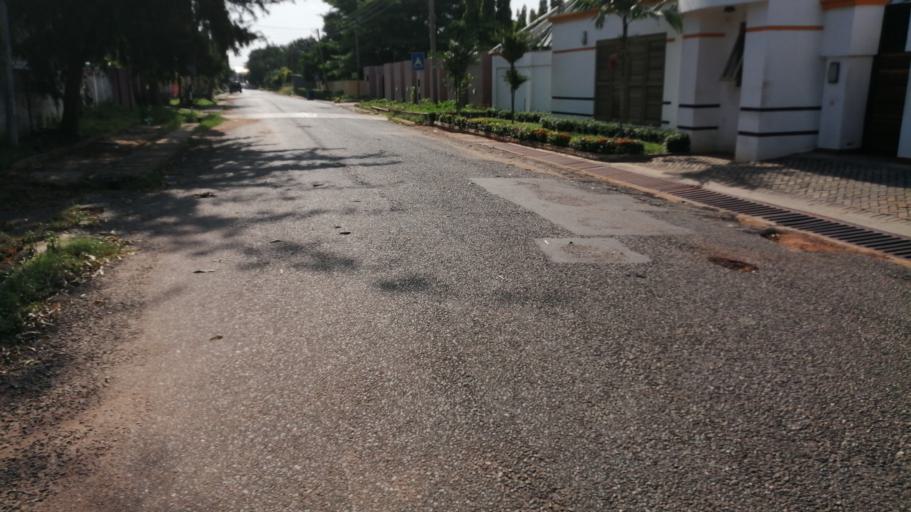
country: GH
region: Greater Accra
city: Medina Estates
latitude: 5.6182
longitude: -0.1819
